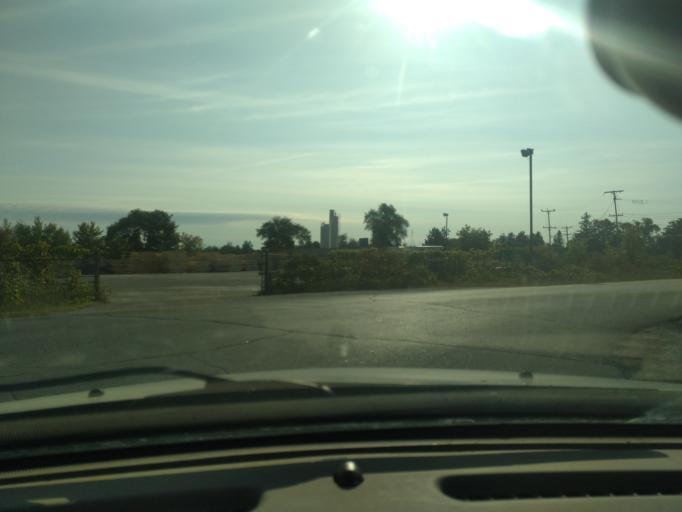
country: CA
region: Ontario
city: Barrie
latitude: 44.3578
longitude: -79.6696
